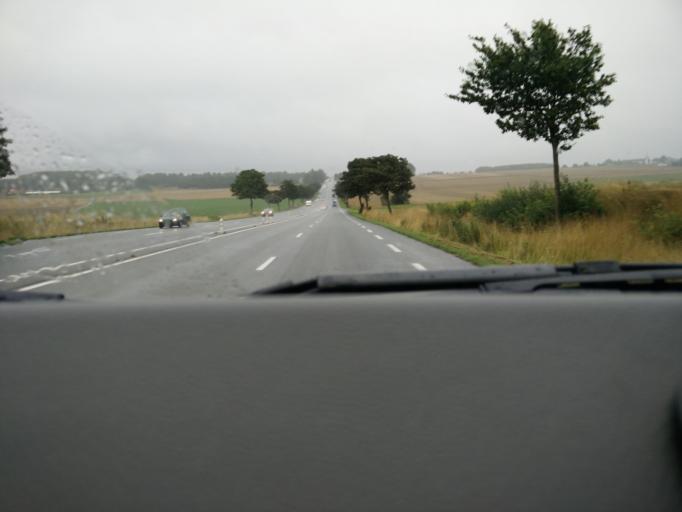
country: FR
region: Nord-Pas-de-Calais
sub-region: Departement du Pas-de-Calais
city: Saint-Pol-sur-Ternoise
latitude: 50.3842
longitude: 2.2605
